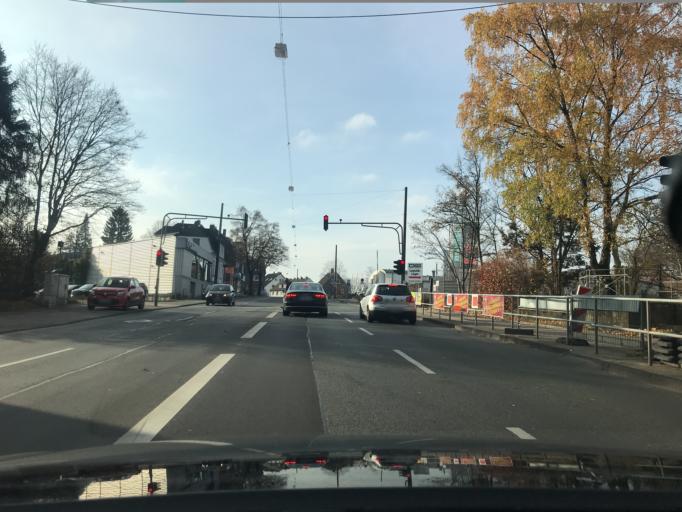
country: DE
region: North Rhine-Westphalia
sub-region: Regierungsbezirk Dusseldorf
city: Remscheid
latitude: 51.2135
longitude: 7.1433
